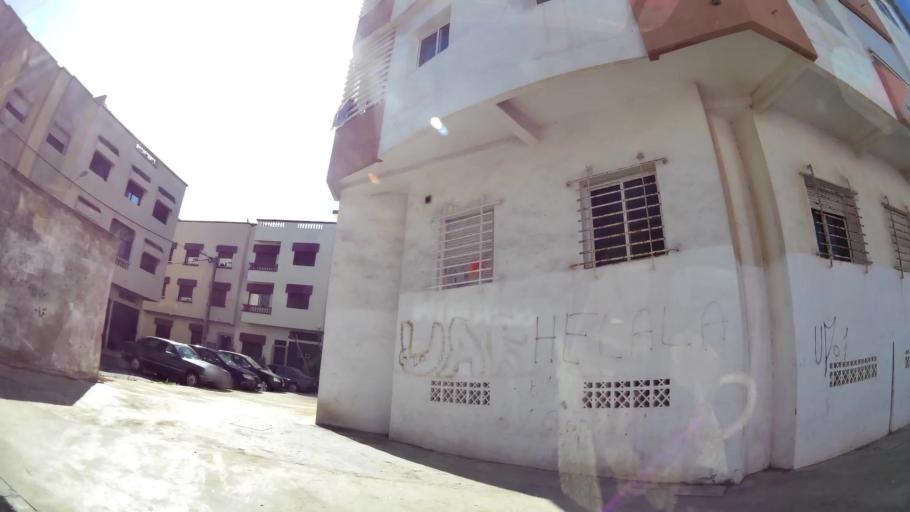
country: MA
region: Rabat-Sale-Zemmour-Zaer
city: Sale
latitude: 34.0701
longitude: -6.7949
